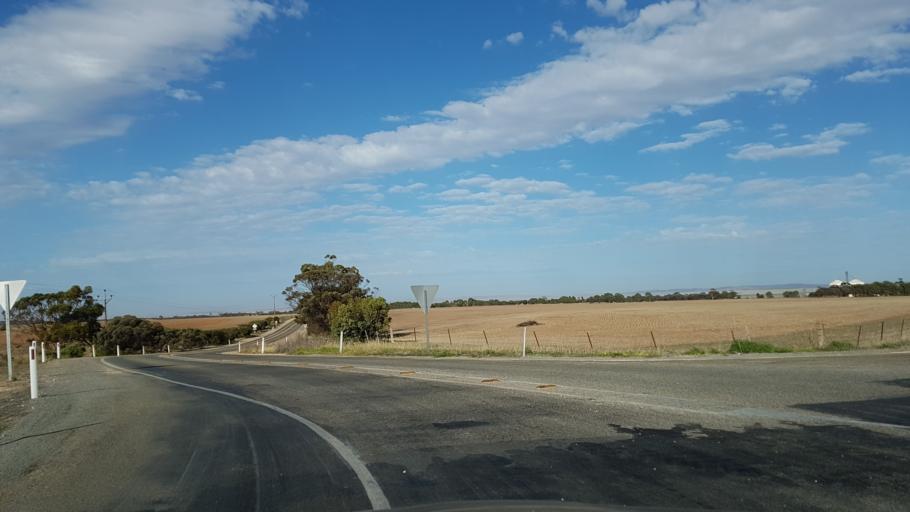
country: AU
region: South Australia
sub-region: Clare and Gilbert Valleys
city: Clare
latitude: -33.6953
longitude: 138.4172
